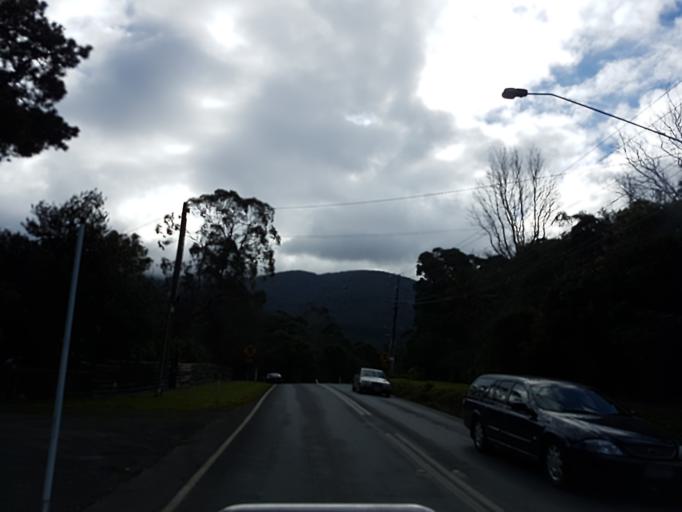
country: AU
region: Victoria
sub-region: Yarra Ranges
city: Millgrove
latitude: -37.7568
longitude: 145.6532
